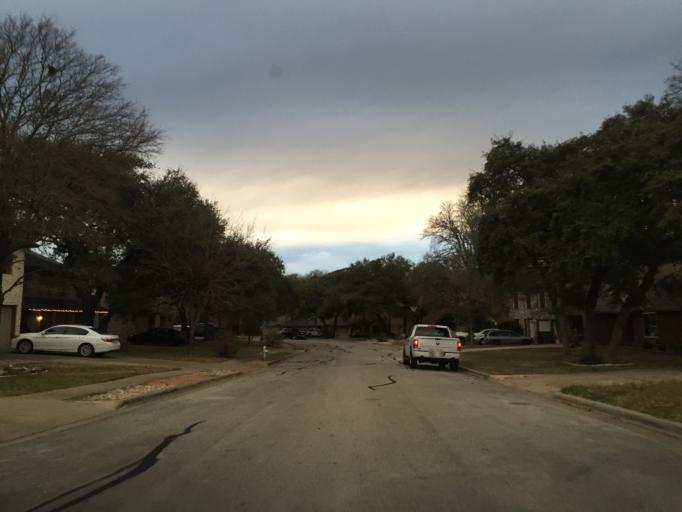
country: US
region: Texas
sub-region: Williamson County
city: Jollyville
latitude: 30.4501
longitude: -97.7511
